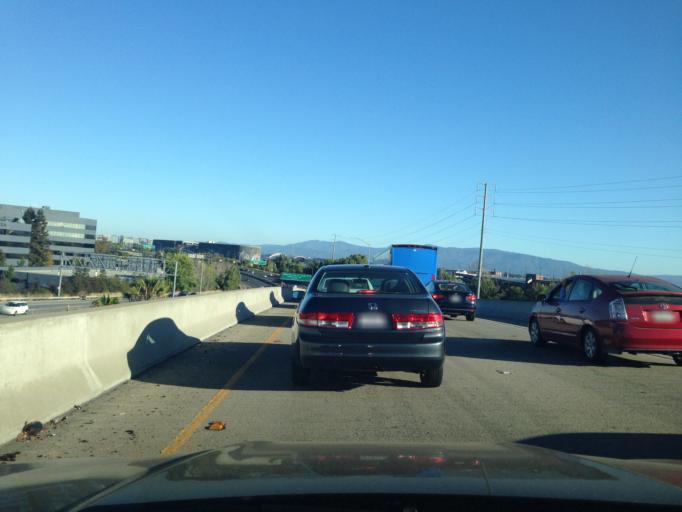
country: US
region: California
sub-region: Santa Clara County
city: Santa Clara
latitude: 37.3733
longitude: -121.9280
